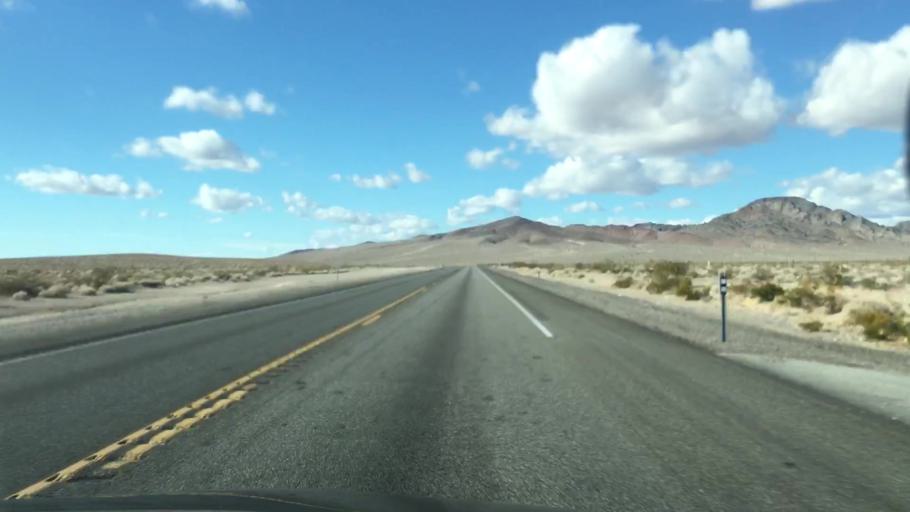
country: US
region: Nevada
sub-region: Nye County
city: Beatty
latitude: 36.6271
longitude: -116.3111
